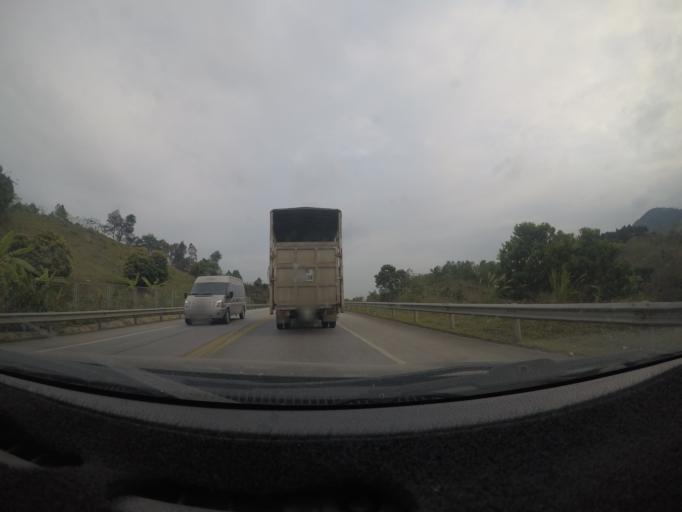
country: VN
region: Yen Bai
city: Thi Tran Yen The
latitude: 21.9973
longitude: 104.5479
